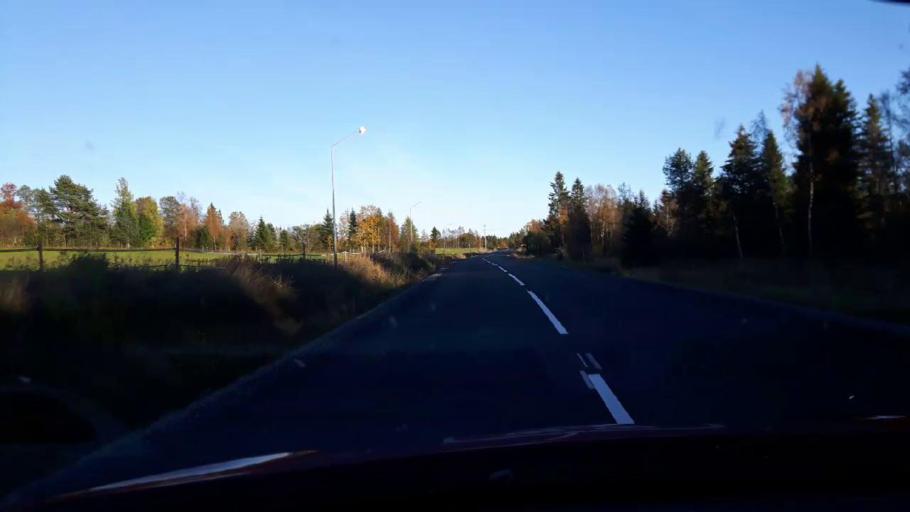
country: SE
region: Jaemtland
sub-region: OEstersunds Kommun
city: Lit
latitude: 63.4320
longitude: 14.8483
